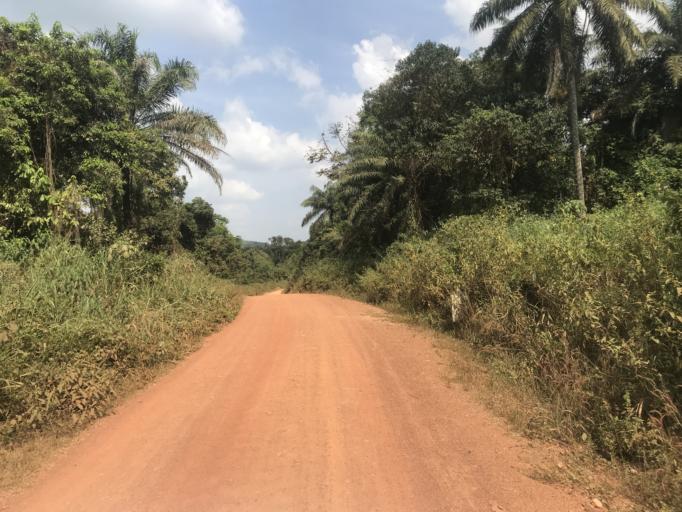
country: NG
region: Osun
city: Inisa
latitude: 7.8858
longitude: 4.3926
